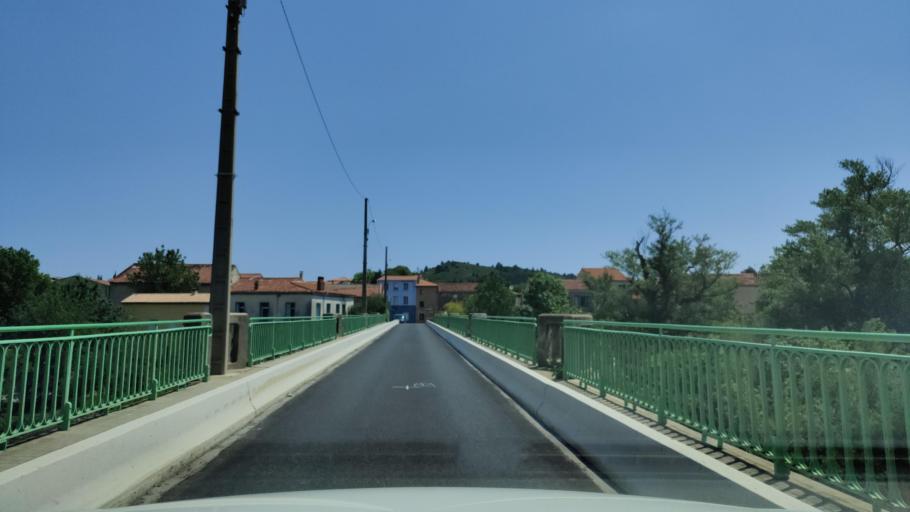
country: FR
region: Languedoc-Roussillon
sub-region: Departement des Pyrenees-Orientales
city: Baixas
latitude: 42.7788
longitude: 2.7881
